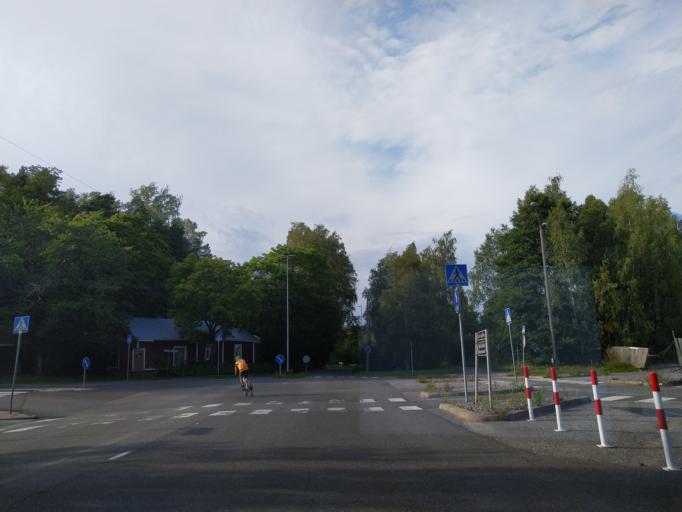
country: FI
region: Varsinais-Suomi
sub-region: Turku
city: Turku
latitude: 60.4269
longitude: 22.2260
